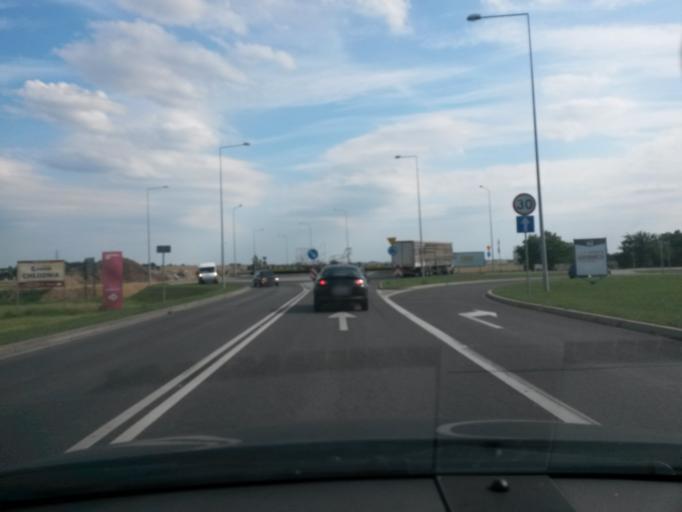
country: PL
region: Greater Poland Voivodeship
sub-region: Powiat gostynski
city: Gostyn
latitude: 51.8513
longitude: 17.0137
